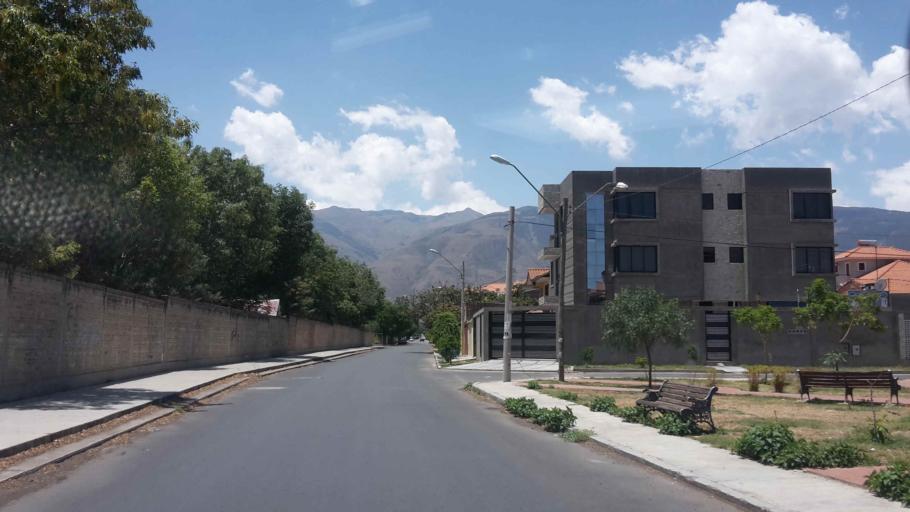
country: BO
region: Cochabamba
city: Cochabamba
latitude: -17.3816
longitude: -66.1920
